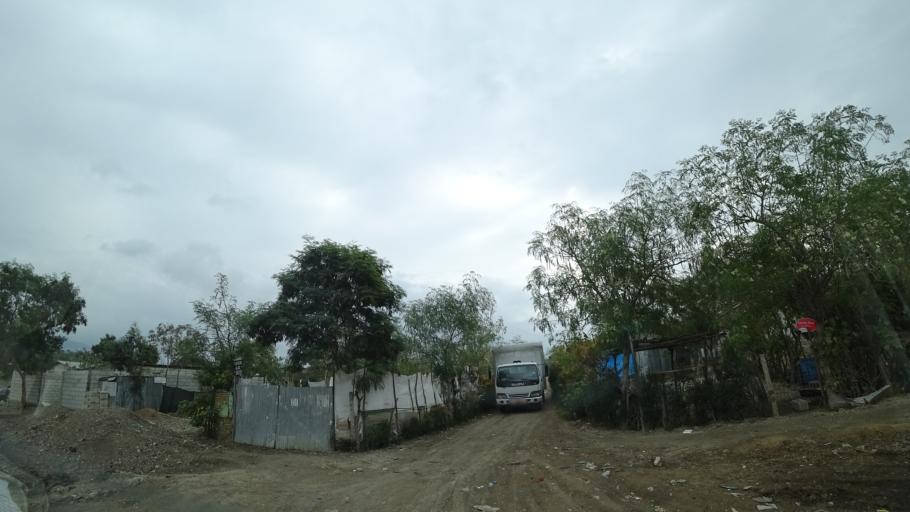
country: HT
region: Ouest
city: Croix des Bouquets
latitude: 18.6497
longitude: -72.2759
